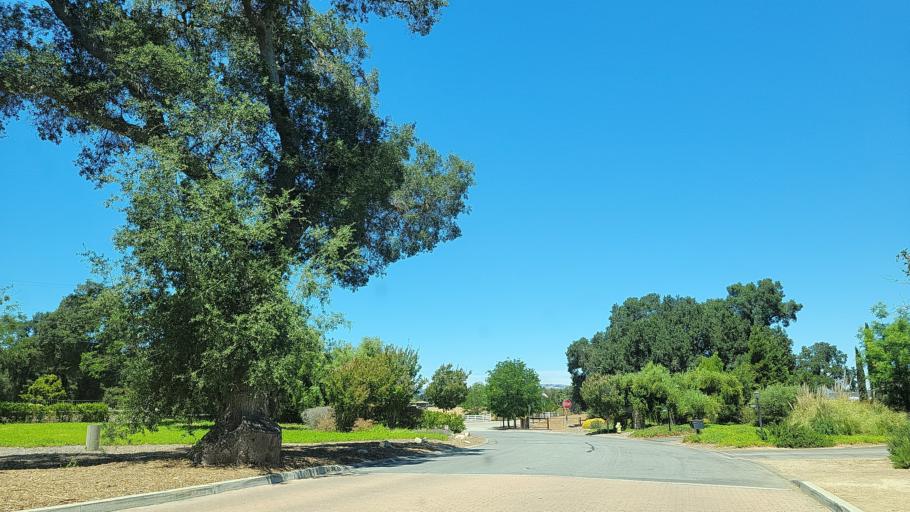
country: US
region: California
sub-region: San Luis Obispo County
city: Atascadero
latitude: 35.5150
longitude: -120.6786
